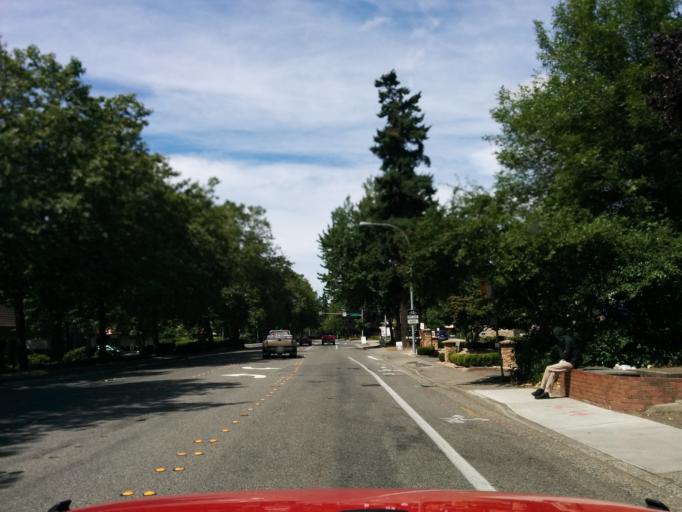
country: US
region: Washington
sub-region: King County
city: Redmond
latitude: 47.6728
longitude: -122.1117
